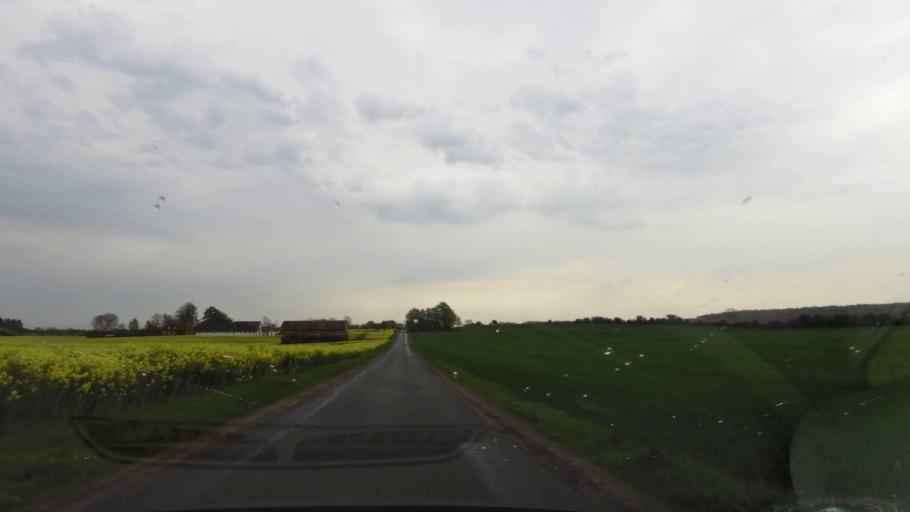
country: DK
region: South Denmark
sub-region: Faaborg-Midtfyn Kommune
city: Ringe
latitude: 55.1910
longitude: 10.5592
